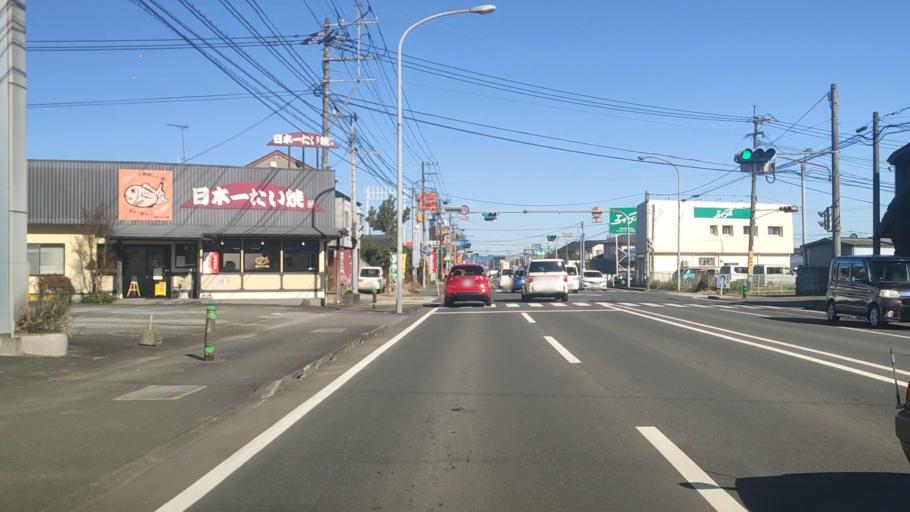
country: JP
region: Miyazaki
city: Miyakonojo
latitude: 31.7436
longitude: 131.0749
